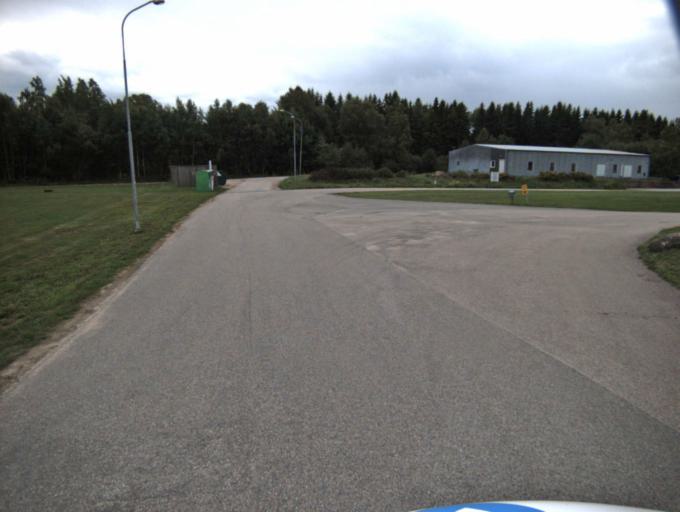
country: SE
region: Vaestra Goetaland
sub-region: Ulricehamns Kommun
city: Ulricehamn
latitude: 57.8412
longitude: 13.2809
